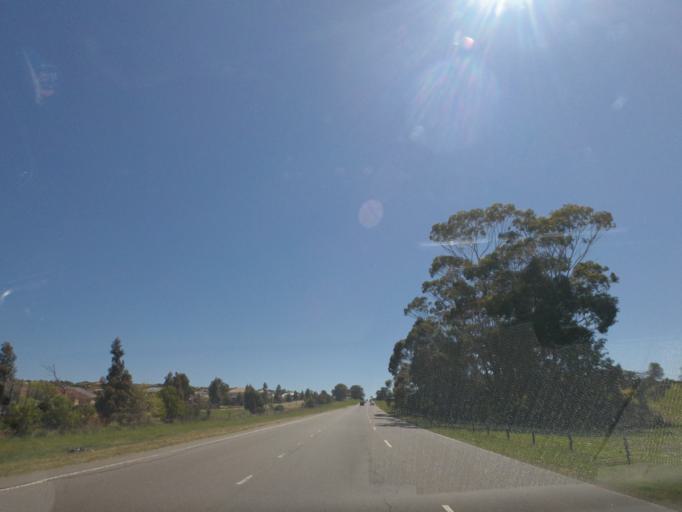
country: AU
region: Victoria
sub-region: Hume
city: Craigieburn
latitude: -37.5761
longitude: 144.9393
